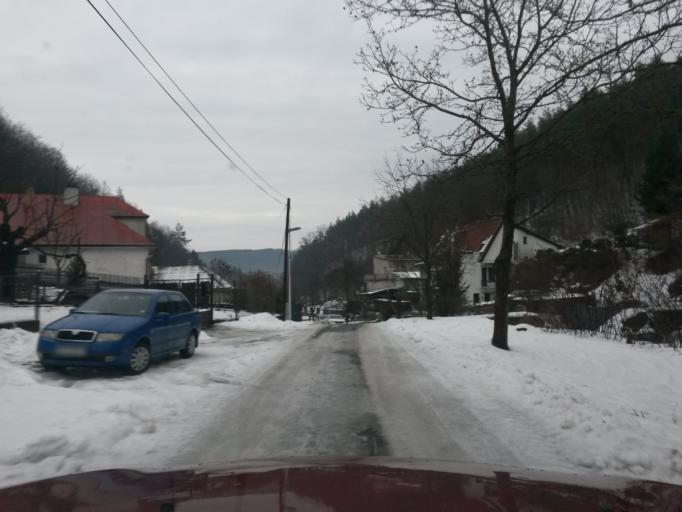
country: SK
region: Kosicky
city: Kosice
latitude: 48.7942
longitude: 21.2336
